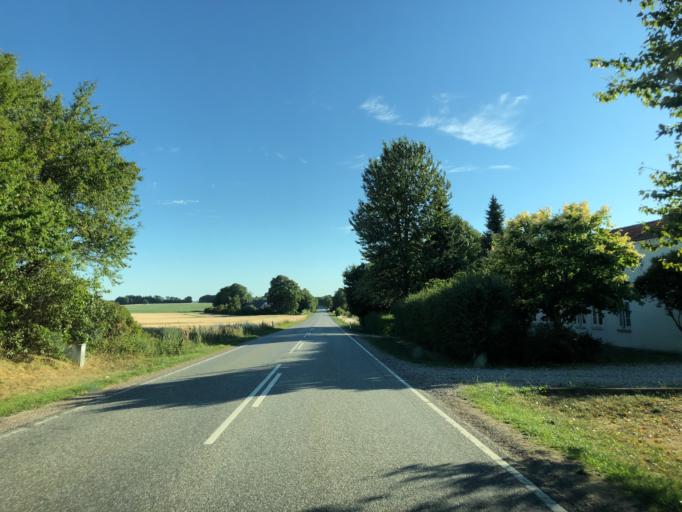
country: DK
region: Central Jutland
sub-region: Skanderborg Kommune
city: Ry
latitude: 56.0087
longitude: 9.7835
